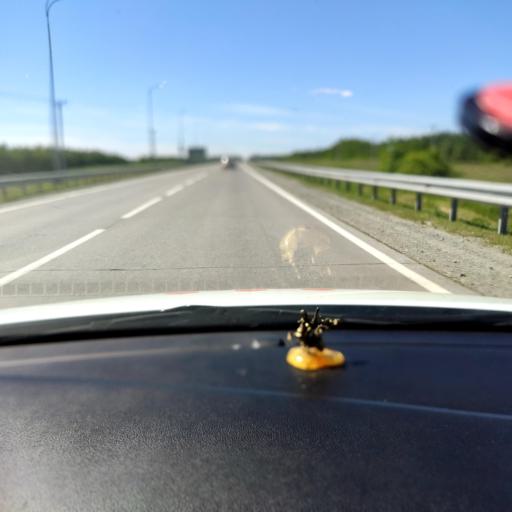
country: RU
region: Tatarstan
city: Stolbishchi
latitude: 55.6767
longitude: 49.1903
